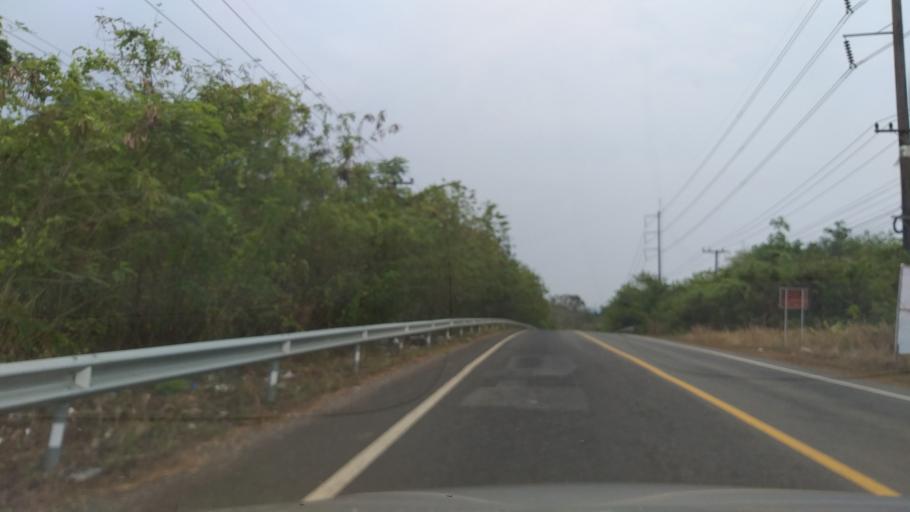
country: TH
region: Trat
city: Laem Ngop
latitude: 12.2634
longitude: 102.2988
